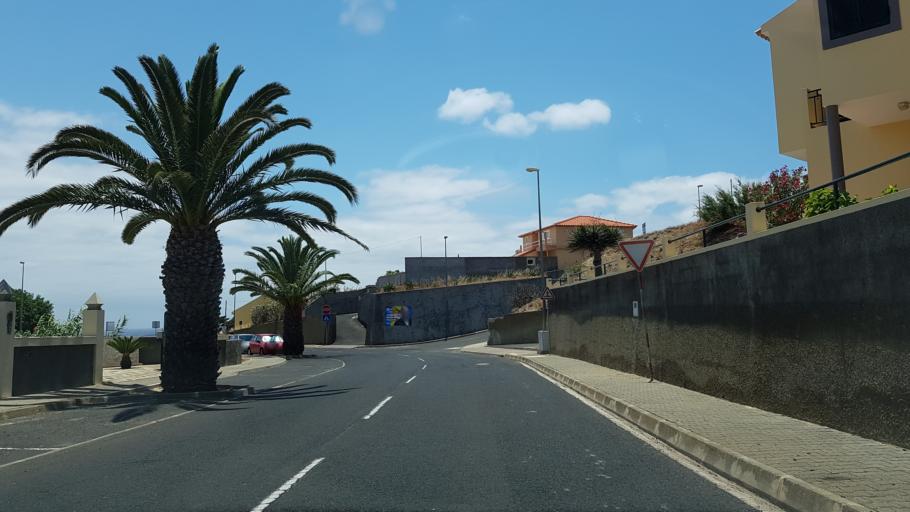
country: PT
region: Madeira
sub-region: Porto Santo
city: Vila de Porto Santo
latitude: 33.0617
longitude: -16.3437
